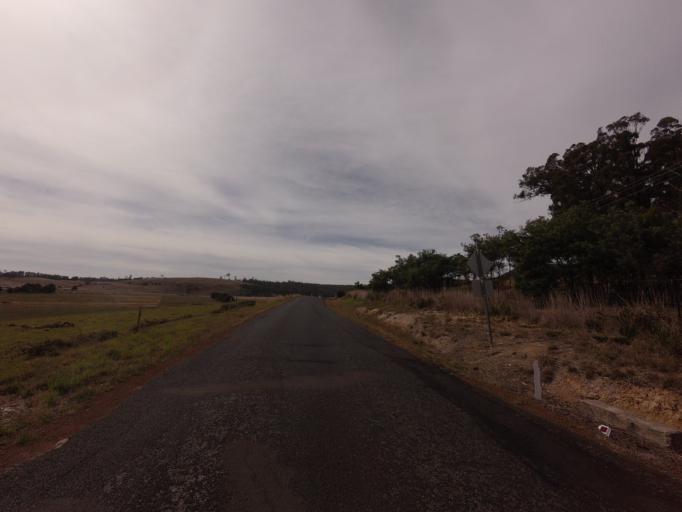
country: AU
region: Tasmania
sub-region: Sorell
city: Sorell
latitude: -42.4278
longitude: 147.5148
